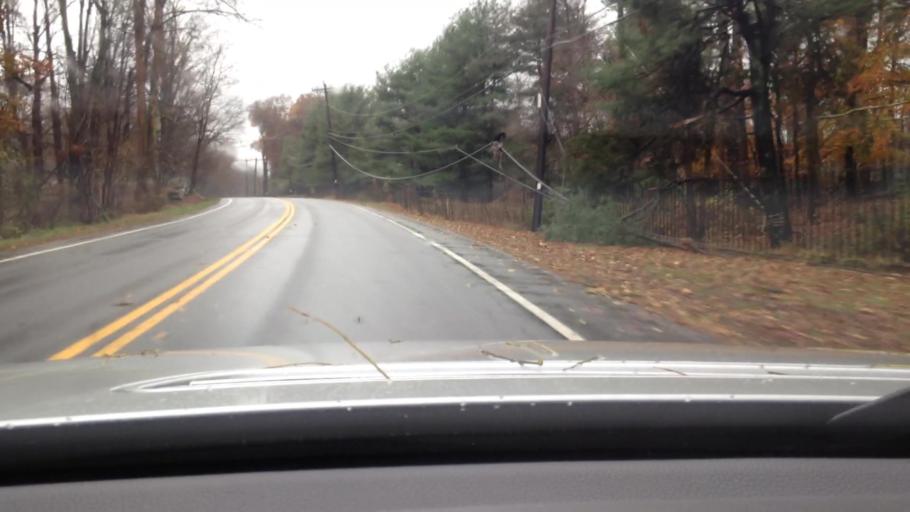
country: US
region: New York
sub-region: Orange County
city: West Point
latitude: 41.3949
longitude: -73.9338
